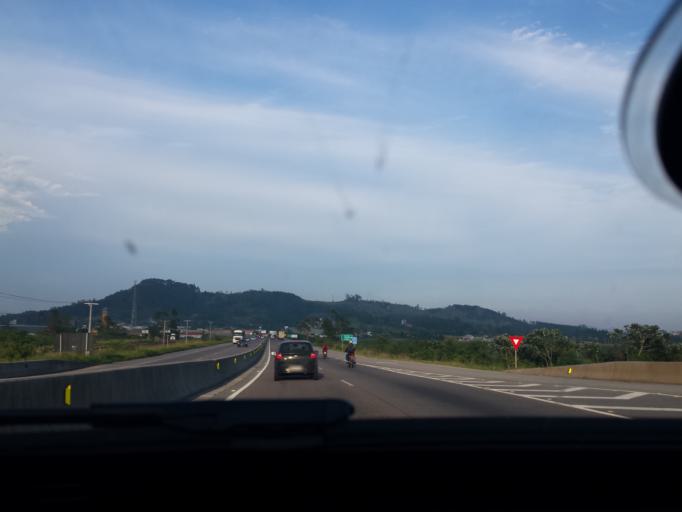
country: BR
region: Santa Catarina
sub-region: Tubarao
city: Tubarao
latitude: -28.4250
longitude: -48.9329
